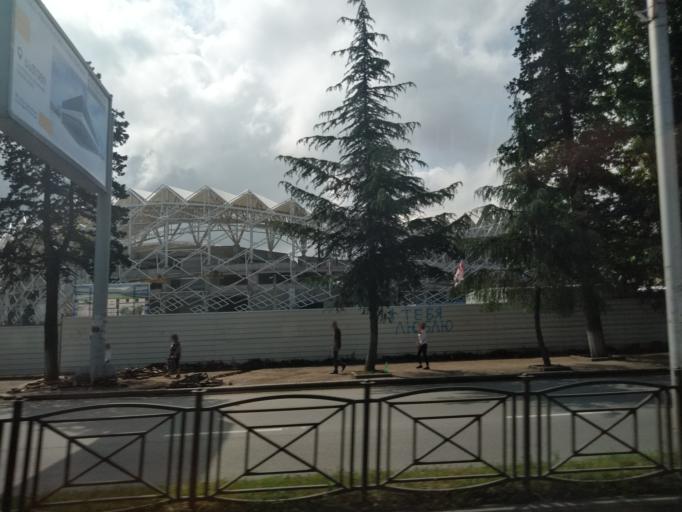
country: GE
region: Ajaria
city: Batumi
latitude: 41.6366
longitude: 41.6177
